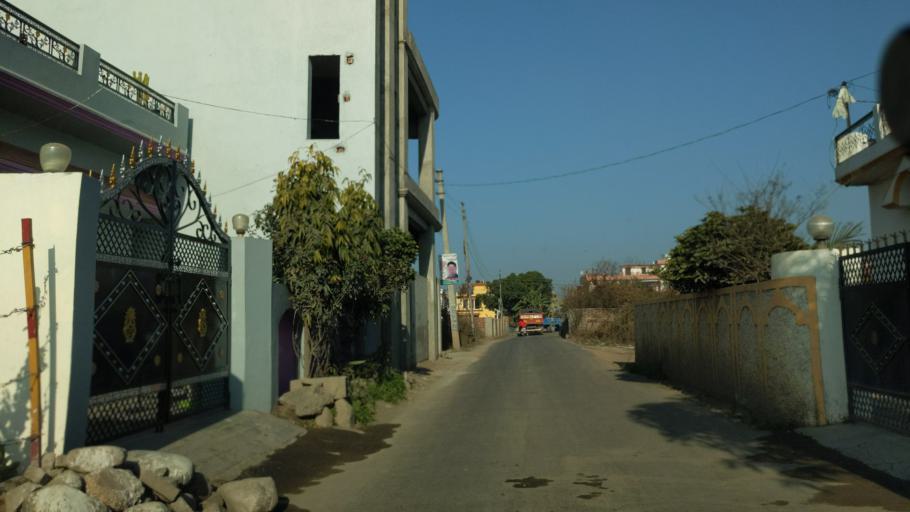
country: IN
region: Uttarakhand
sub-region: Naini Tal
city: Haldwani
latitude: 29.2100
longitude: 79.4915
